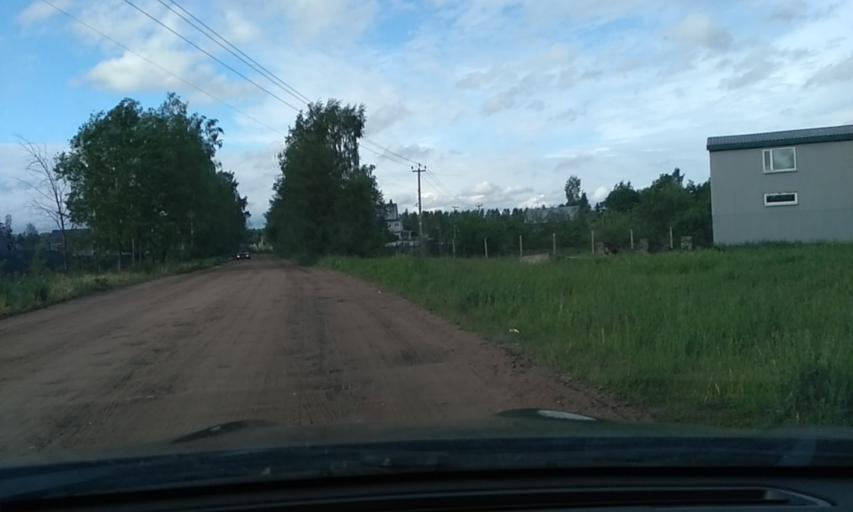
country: RU
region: Leningrad
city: Otradnoye
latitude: 59.8007
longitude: 30.8022
